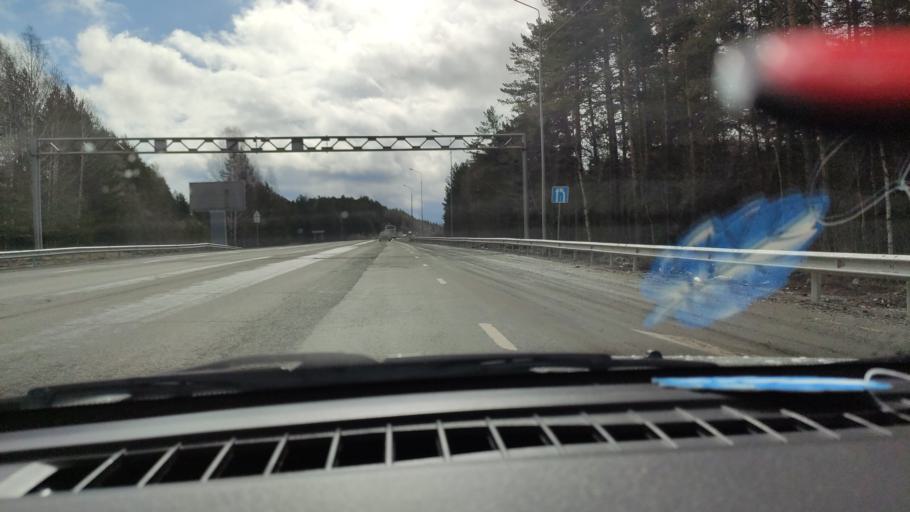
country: RU
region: Sverdlovsk
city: Talitsa
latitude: 56.8716
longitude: 60.0377
